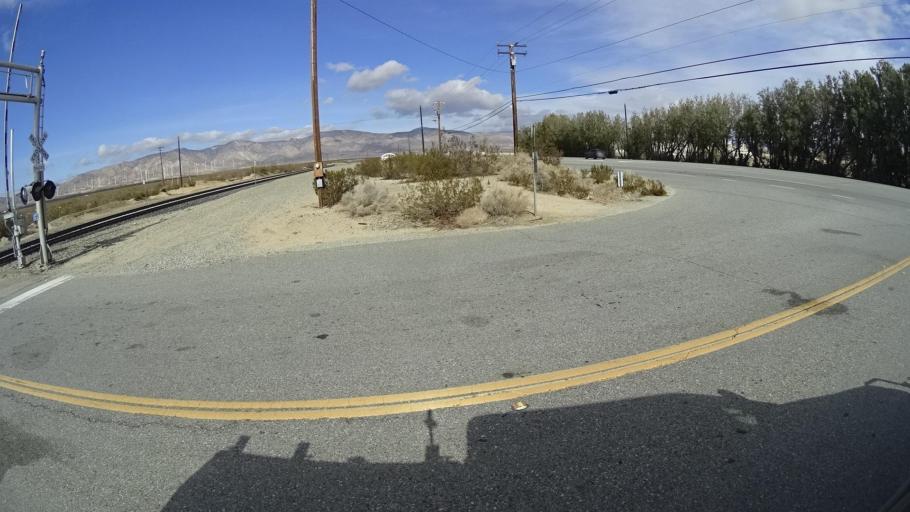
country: US
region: California
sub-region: Kern County
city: Mojave
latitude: 35.0686
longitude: -118.1793
